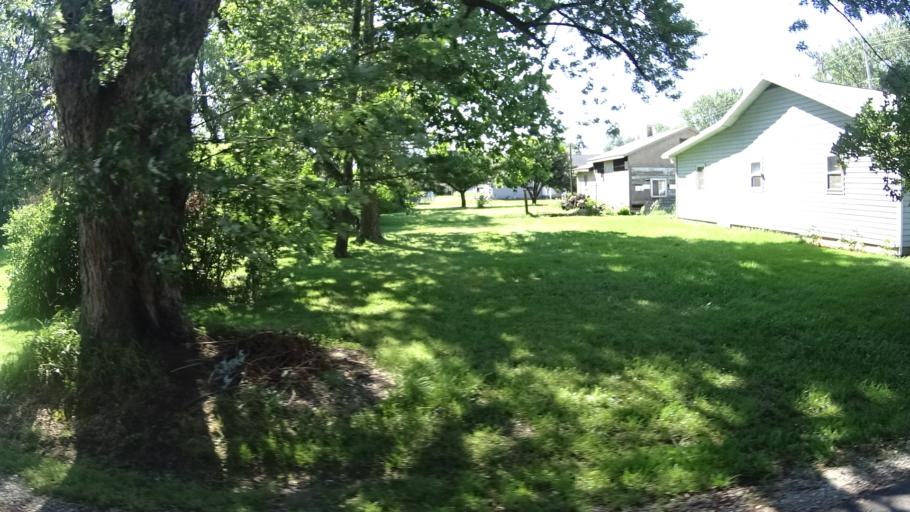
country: US
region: Ohio
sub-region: Erie County
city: Sandusky
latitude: 41.4704
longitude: -82.8244
